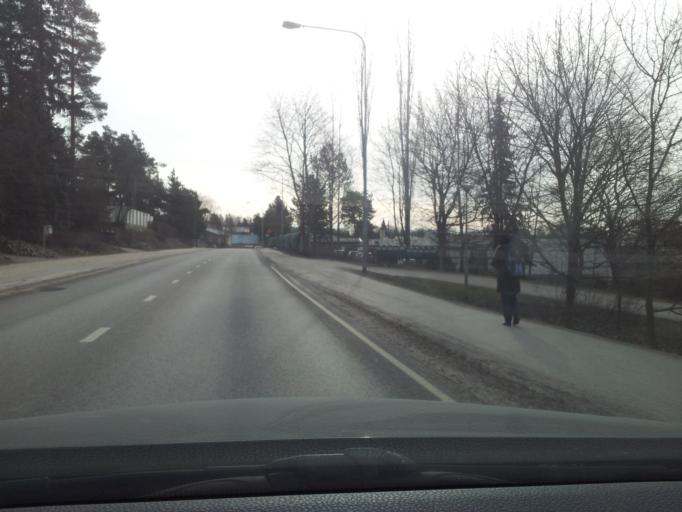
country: FI
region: Uusimaa
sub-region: Helsinki
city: Kilo
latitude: 60.1934
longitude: 24.7716
